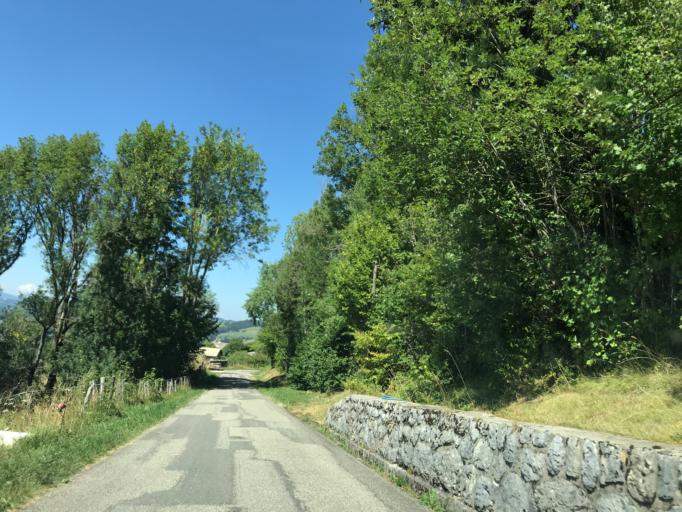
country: FR
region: Rhone-Alpes
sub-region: Departement de la Haute-Savoie
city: Thorens-Glieres
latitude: 45.9768
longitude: 6.2302
